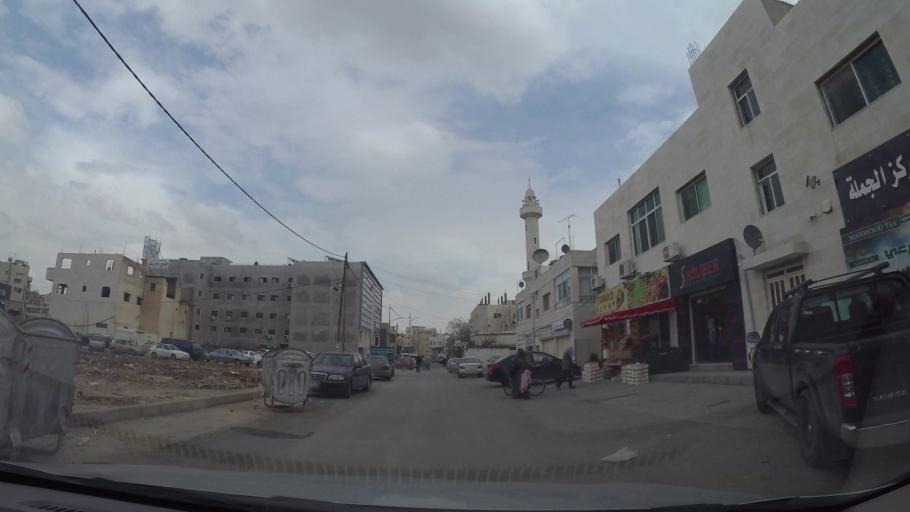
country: JO
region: Amman
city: Umm as Summaq
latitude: 31.8932
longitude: 35.8388
